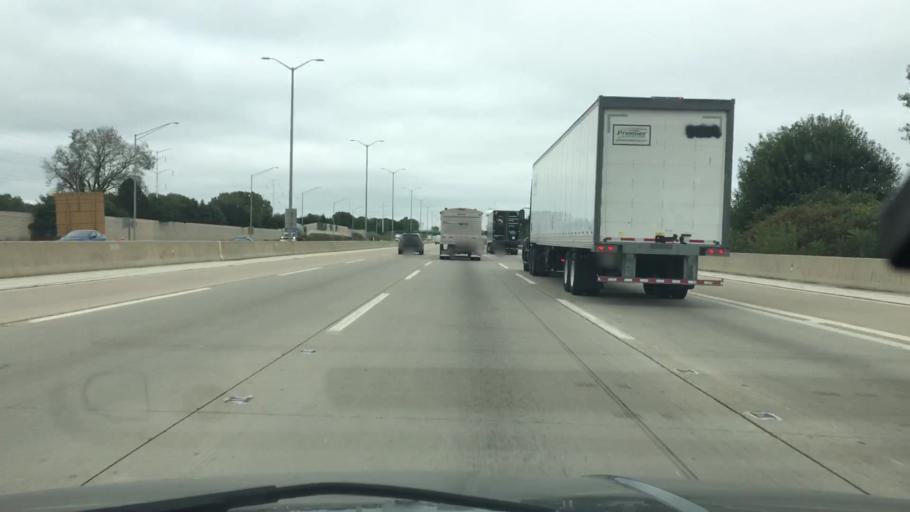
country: US
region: Illinois
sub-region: DuPage County
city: Oakbrook Terrace
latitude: 41.8450
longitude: -87.9625
